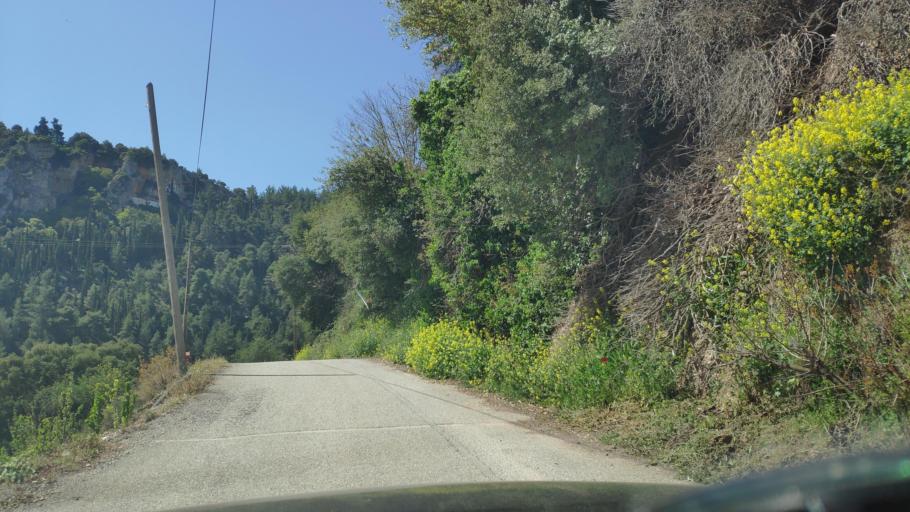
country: GR
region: West Greece
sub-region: Nomos Achaias
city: Akrata
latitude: 38.0975
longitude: 22.3190
